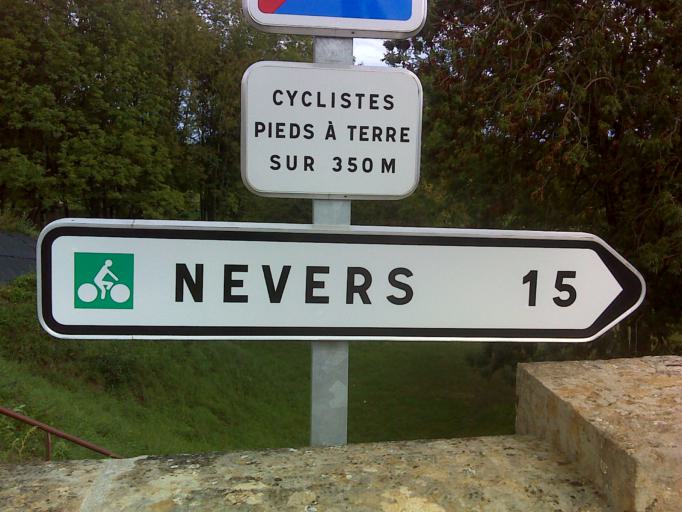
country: FR
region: Centre
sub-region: Departement du Cher
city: Cuffy
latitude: 46.9469
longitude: 3.0695
